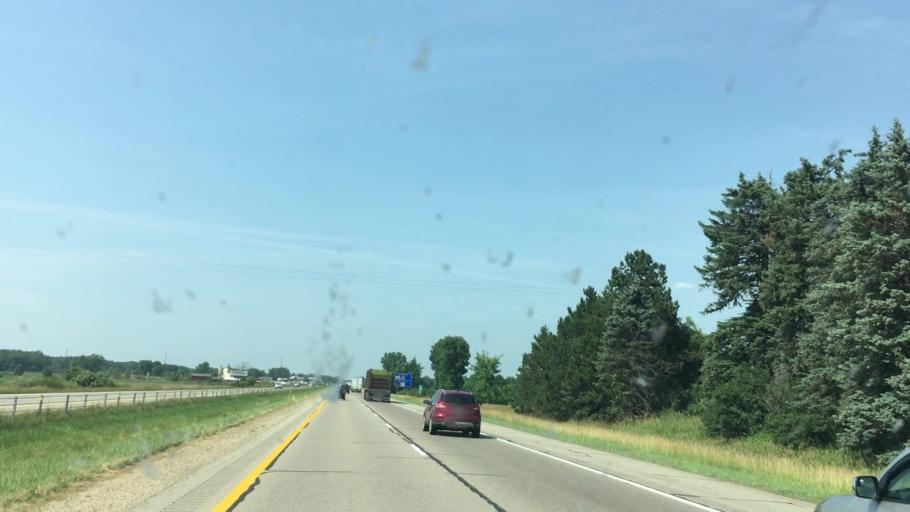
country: US
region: Michigan
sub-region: Allegan County
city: Wayland
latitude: 42.6515
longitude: -85.6620
